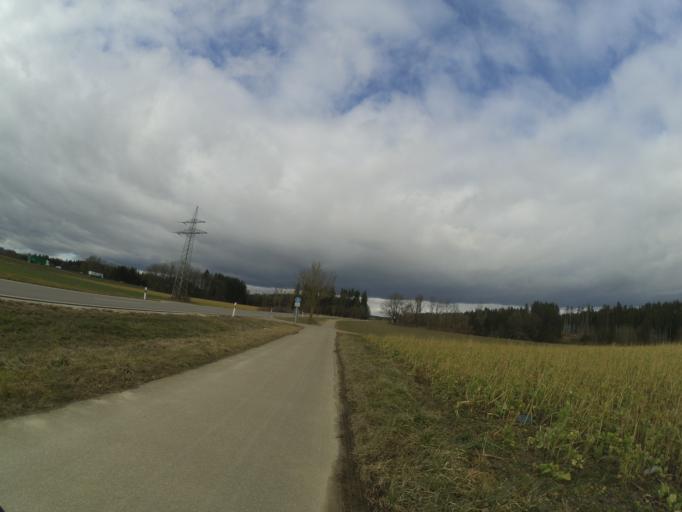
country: DE
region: Bavaria
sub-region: Swabia
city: Vohringen
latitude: 48.3058
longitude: 10.1047
